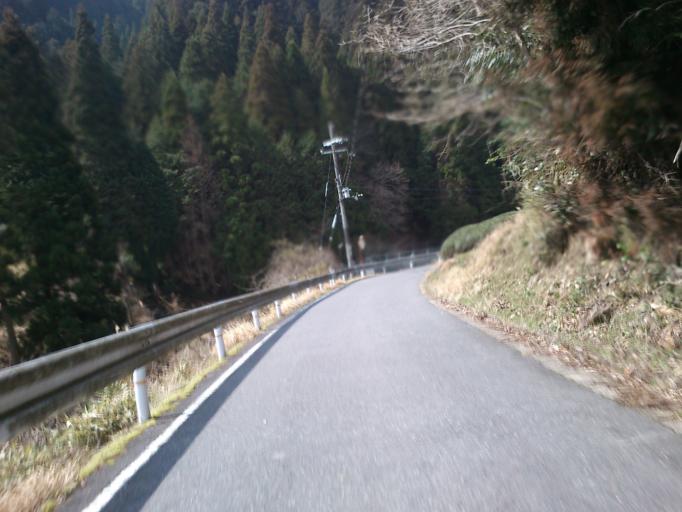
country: JP
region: Kyoto
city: Uji
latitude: 34.8256
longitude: 135.9663
